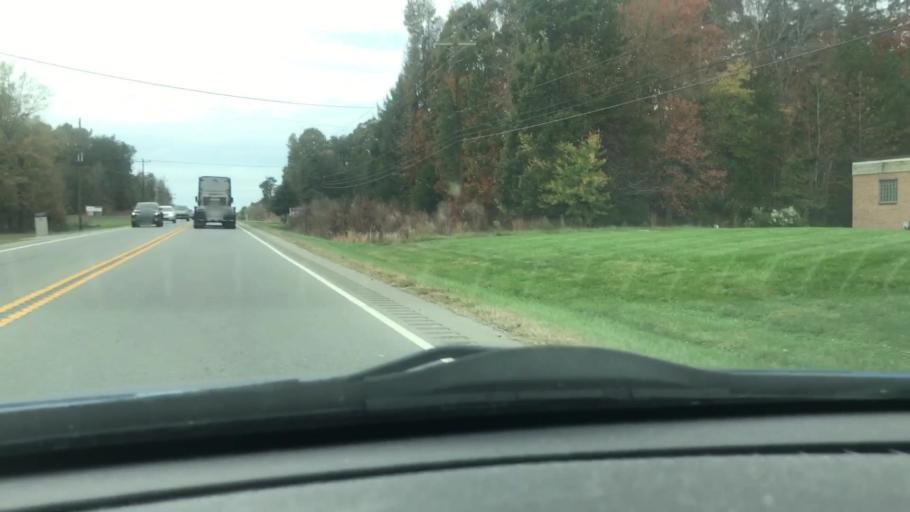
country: US
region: North Carolina
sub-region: Davidson County
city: Thomasville
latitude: 35.7949
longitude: -80.1464
